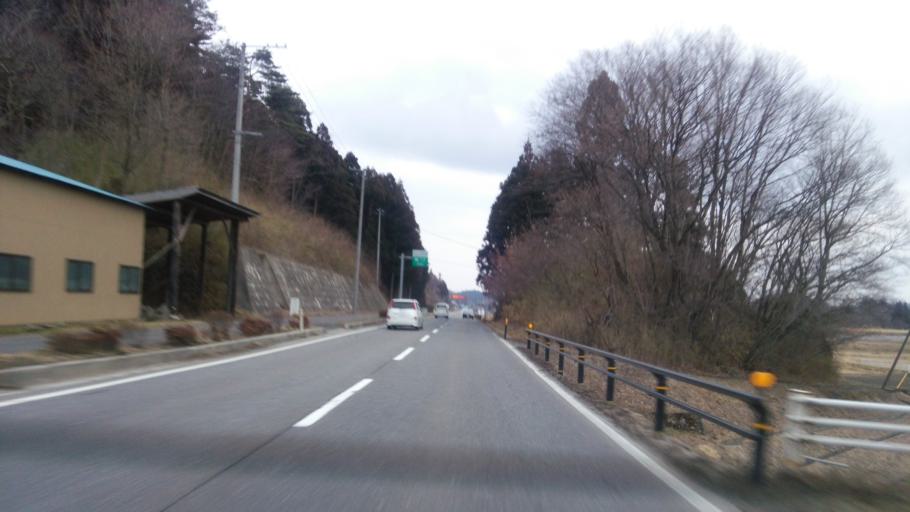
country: JP
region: Fukushima
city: Ishikawa
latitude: 37.2649
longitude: 140.5553
